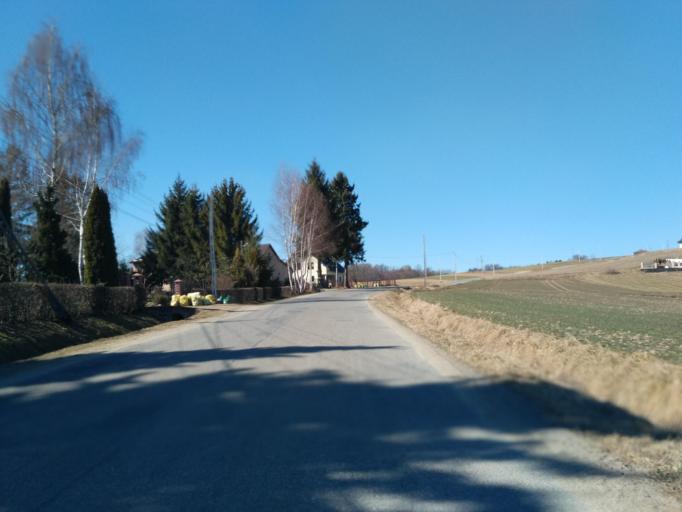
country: PL
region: Subcarpathian Voivodeship
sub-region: Powiat debicki
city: Brzostek
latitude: 49.9407
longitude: 21.4388
